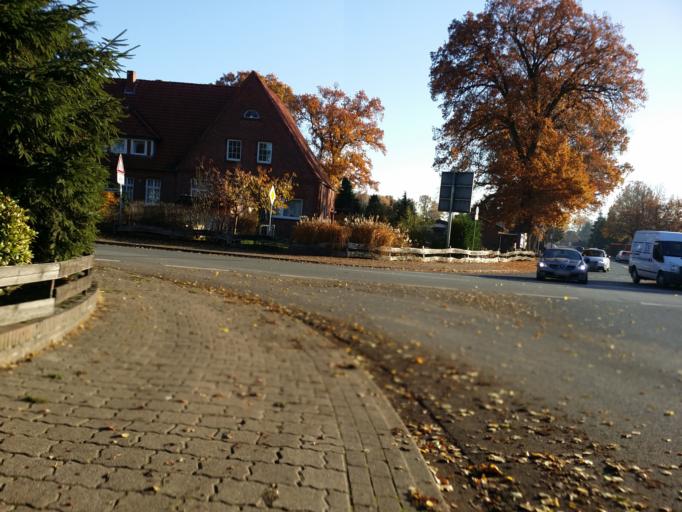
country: DE
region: Lower Saxony
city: Langwedel
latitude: 53.0344
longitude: 9.1563
